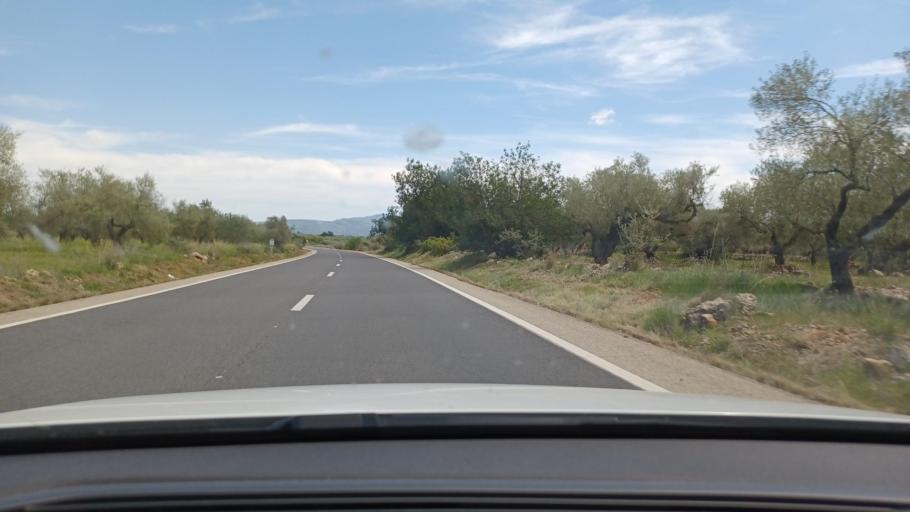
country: ES
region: Catalonia
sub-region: Provincia de Tarragona
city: Mas de Barberans
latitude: 40.6398
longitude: 0.3462
